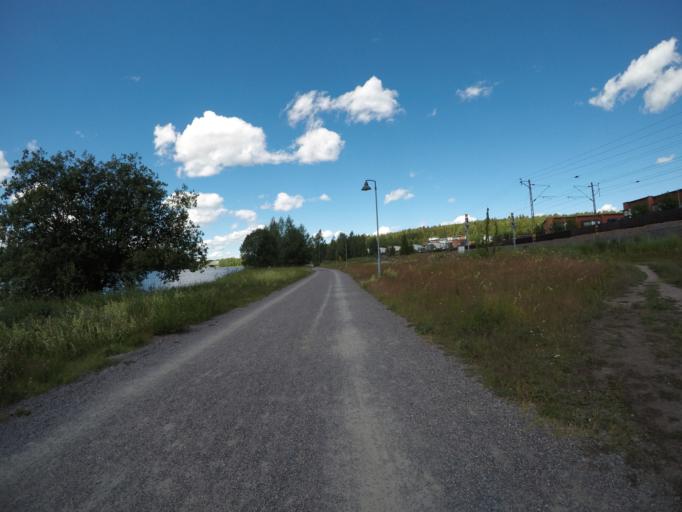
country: FI
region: Haeme
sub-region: Haemeenlinna
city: Haemeenlinna
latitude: 61.0091
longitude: 24.4629
